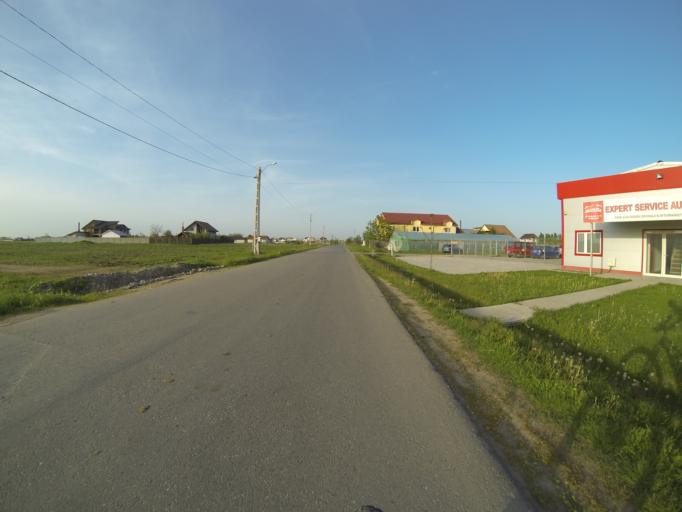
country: RO
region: Dolj
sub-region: Comuna Carcea
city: Carcea
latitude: 44.3235
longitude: 23.8842
